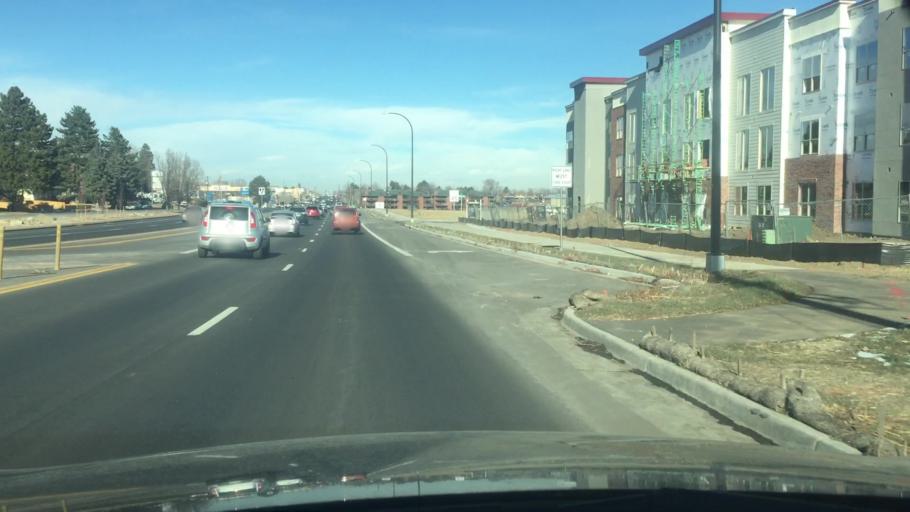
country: US
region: Colorado
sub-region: Jefferson County
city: Lakewood
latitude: 39.6763
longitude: -105.0814
